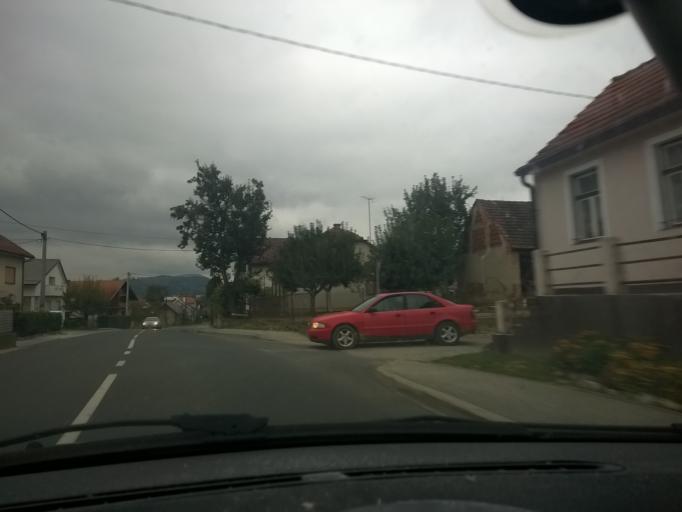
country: HR
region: Krapinsko-Zagorska
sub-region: Grad Krapina
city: Krapina
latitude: 46.1251
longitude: 15.8932
